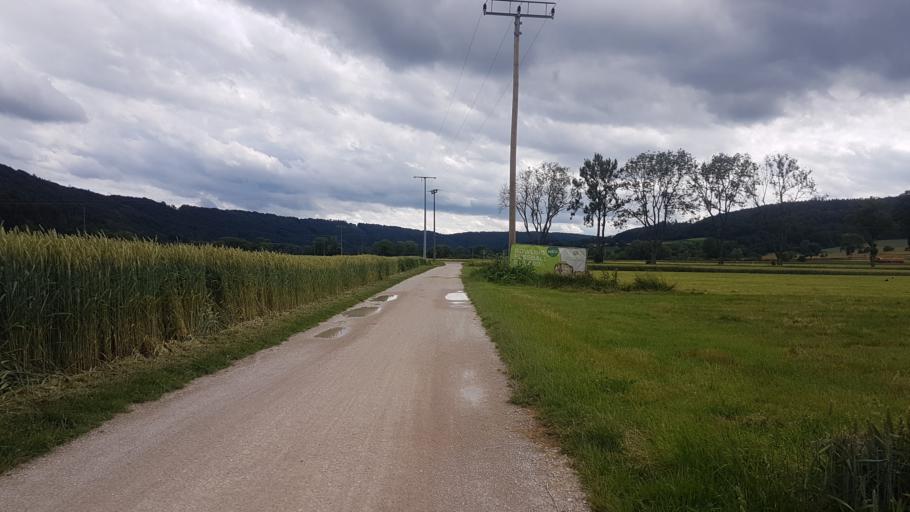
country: DE
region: Bavaria
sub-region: Upper Bavaria
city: Denkendorf
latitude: 49.0193
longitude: 11.4524
